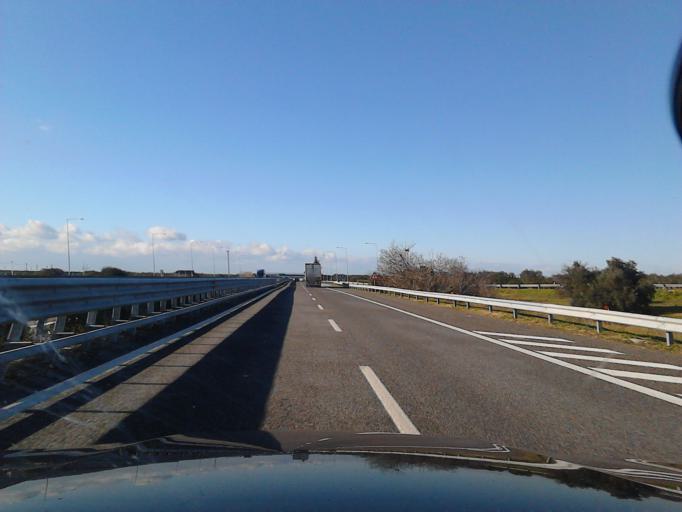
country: IT
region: Apulia
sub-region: Provincia di Foggia
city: Cerignola
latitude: 41.3238
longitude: 15.8974
